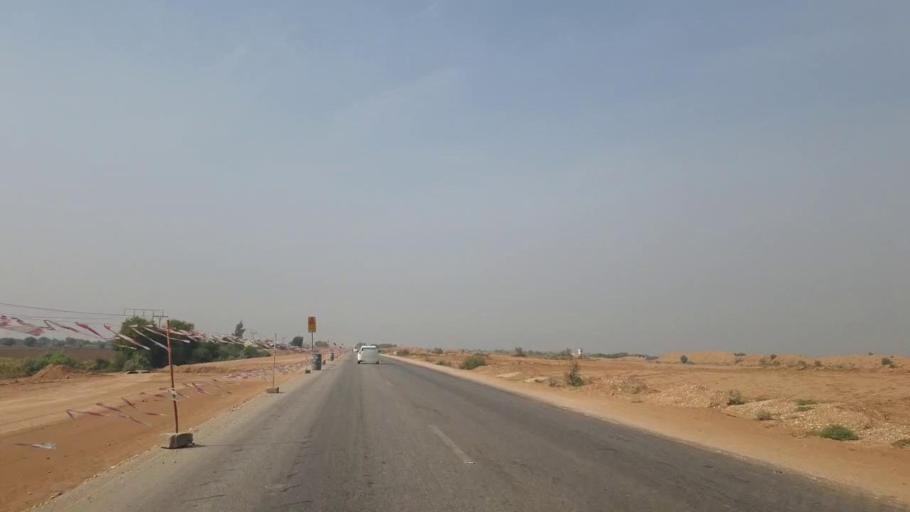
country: PK
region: Sindh
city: Sann
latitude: 26.1284
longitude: 68.0516
